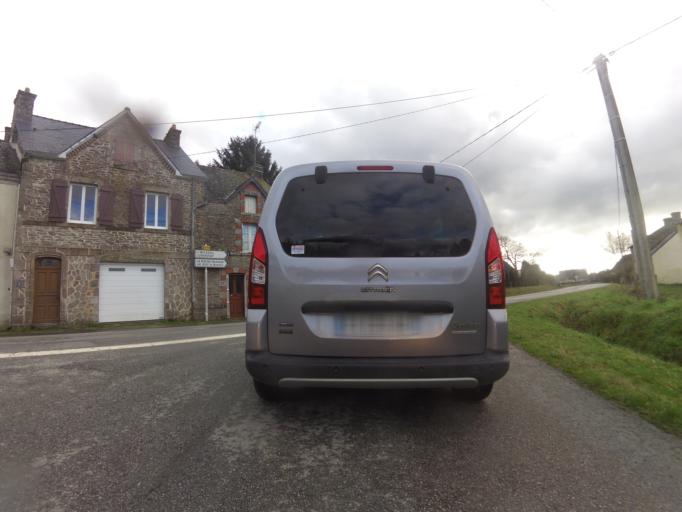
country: FR
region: Brittany
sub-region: Departement du Morbihan
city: Limerzel
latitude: 47.6425
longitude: -2.3603
